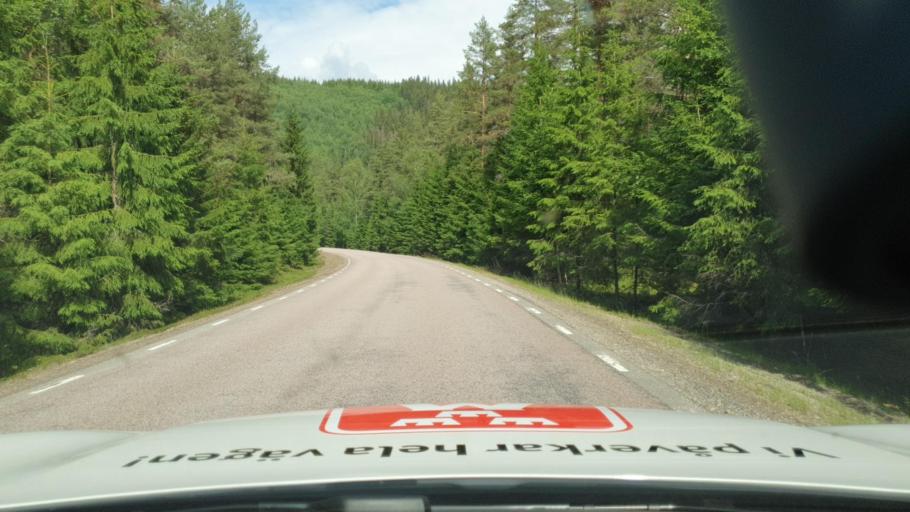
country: SE
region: Vaermland
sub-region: Torsby Kommun
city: Torsby
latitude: 60.7492
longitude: 12.7971
